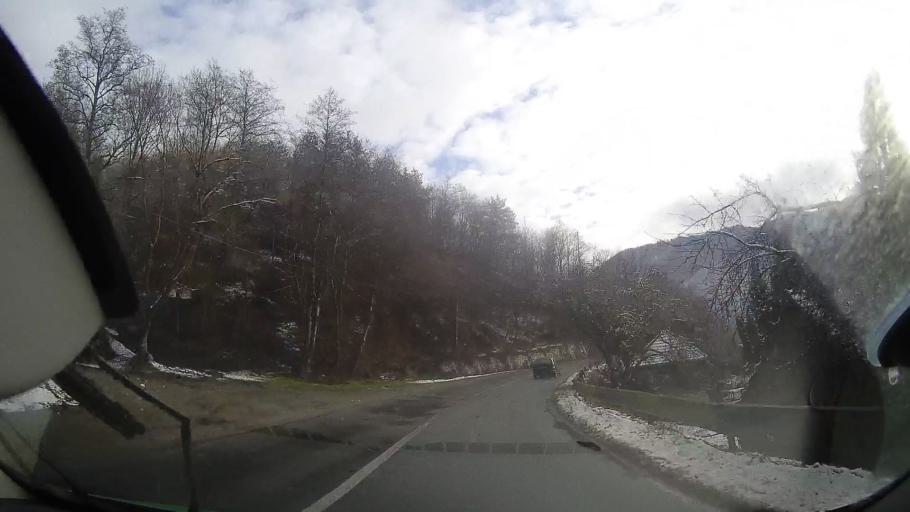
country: RO
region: Alba
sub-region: Oras Baia de Aries
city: Baia de Aries
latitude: 46.4017
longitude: 23.3074
